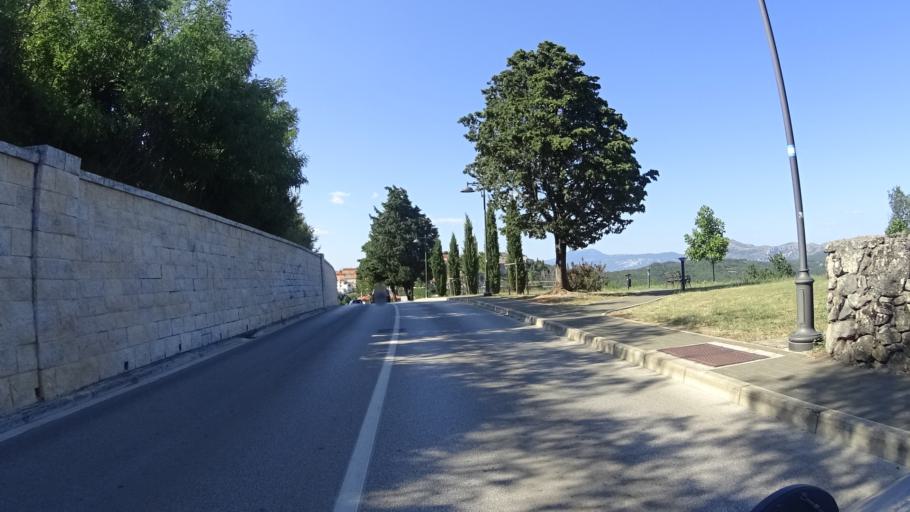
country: HR
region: Istarska
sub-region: Grad Labin
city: Labin
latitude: 45.0809
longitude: 14.1240
